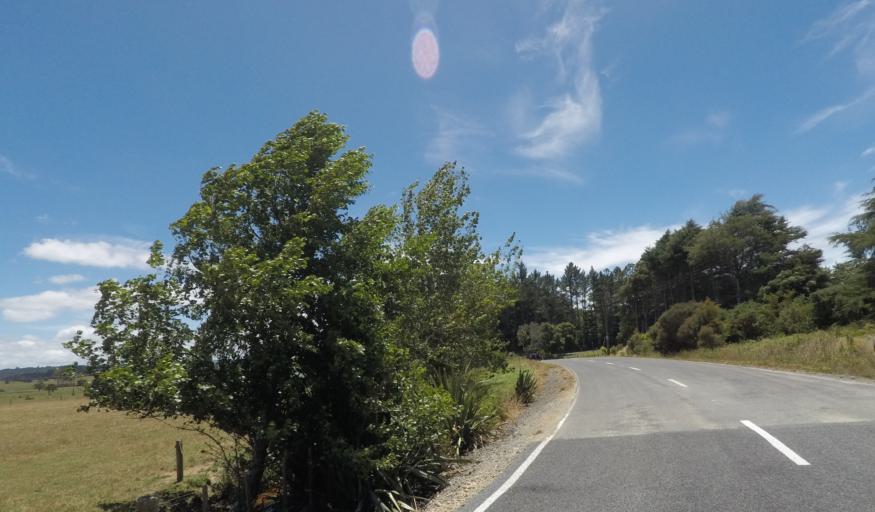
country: NZ
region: Northland
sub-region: Whangarei
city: Whangarei
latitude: -35.5469
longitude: 174.3047
